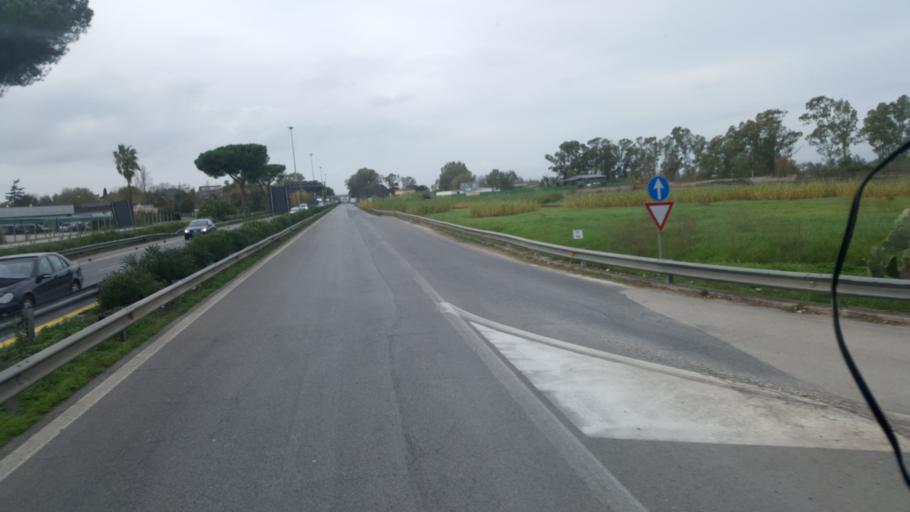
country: IT
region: Latium
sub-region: Provincia di Latina
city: Borgo Podgora
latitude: 41.4859
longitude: 12.8533
